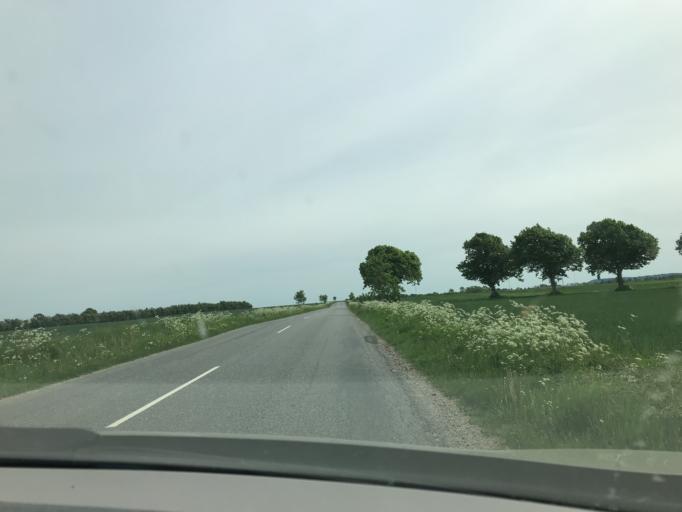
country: DK
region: Central Jutland
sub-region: Norddjurs Kommune
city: Allingabro
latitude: 56.5195
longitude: 10.3267
